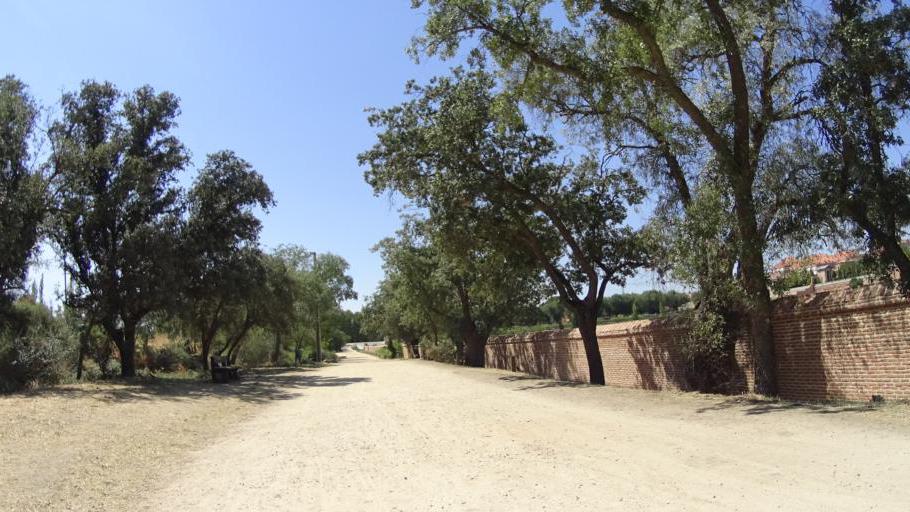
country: ES
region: Madrid
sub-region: Provincia de Madrid
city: Boadilla del Monte
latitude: 40.4056
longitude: -3.8718
